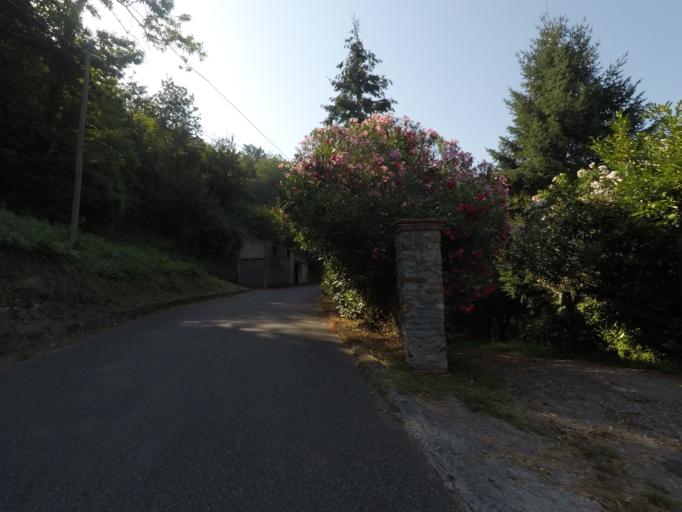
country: IT
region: Tuscany
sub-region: Provincia di Massa-Carrara
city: Carrara
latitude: 44.0730
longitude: 10.0660
